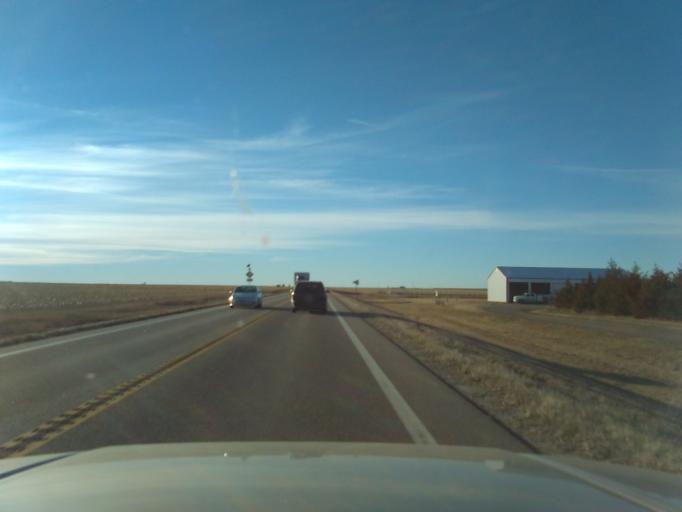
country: US
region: Kansas
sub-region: Thomas County
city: Colby
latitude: 39.4649
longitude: -100.7418
